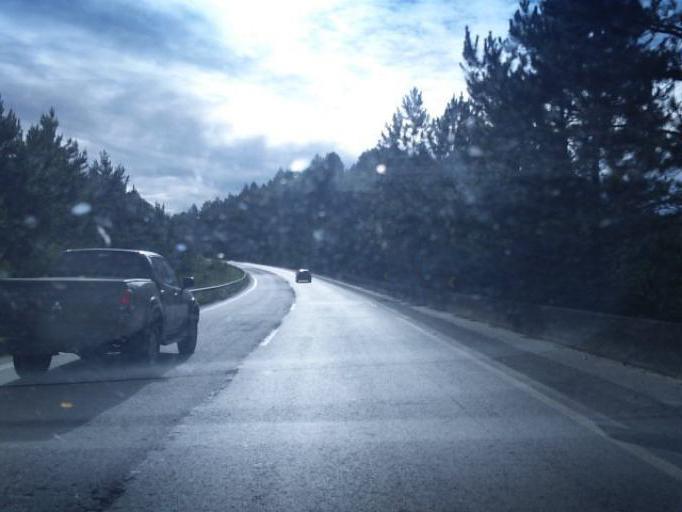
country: BR
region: Parana
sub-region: Campina Grande Do Sul
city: Campina Grande do Sul
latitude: -25.1058
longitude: -48.8468
